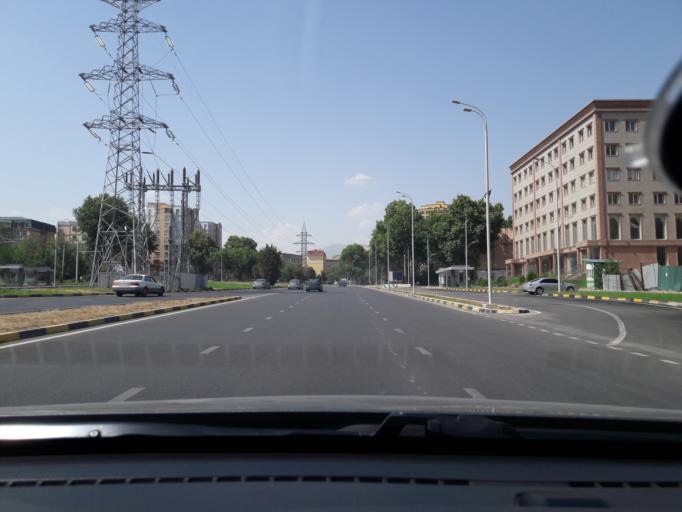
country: TJ
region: Dushanbe
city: Dushanbe
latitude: 38.5858
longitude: 68.7413
